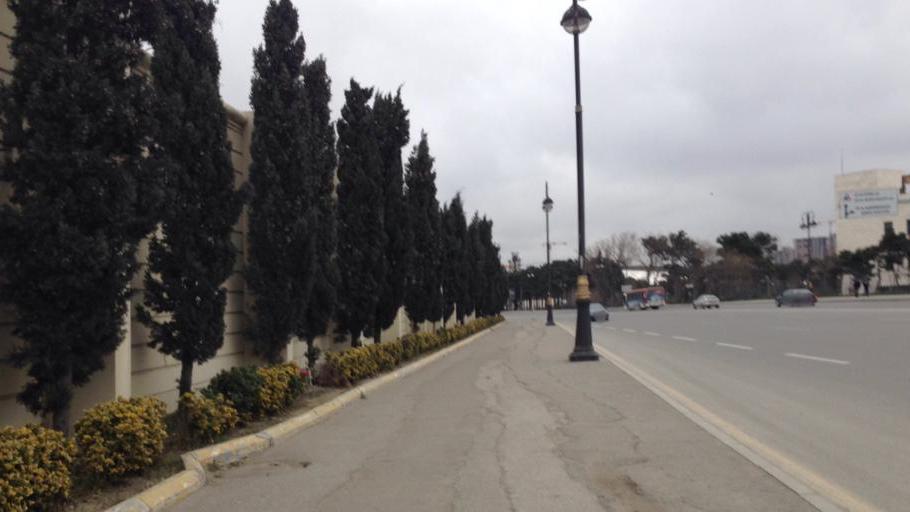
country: AZ
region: Baki
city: Baku
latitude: 40.3944
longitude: 49.8471
